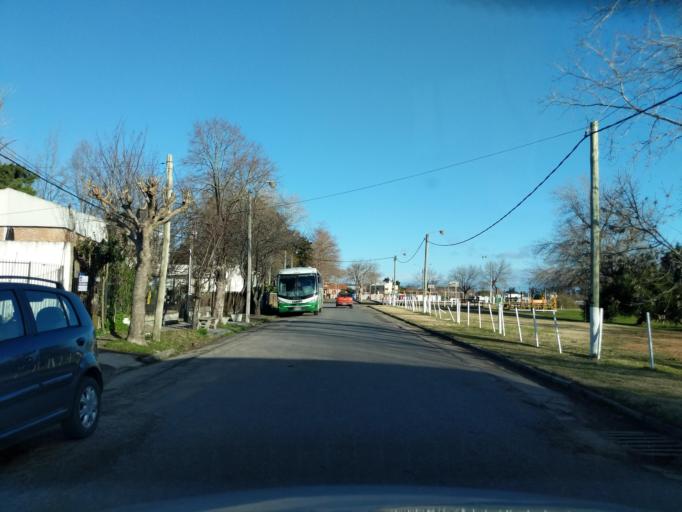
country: UY
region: Florida
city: Florida
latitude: -34.0984
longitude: -56.2227
